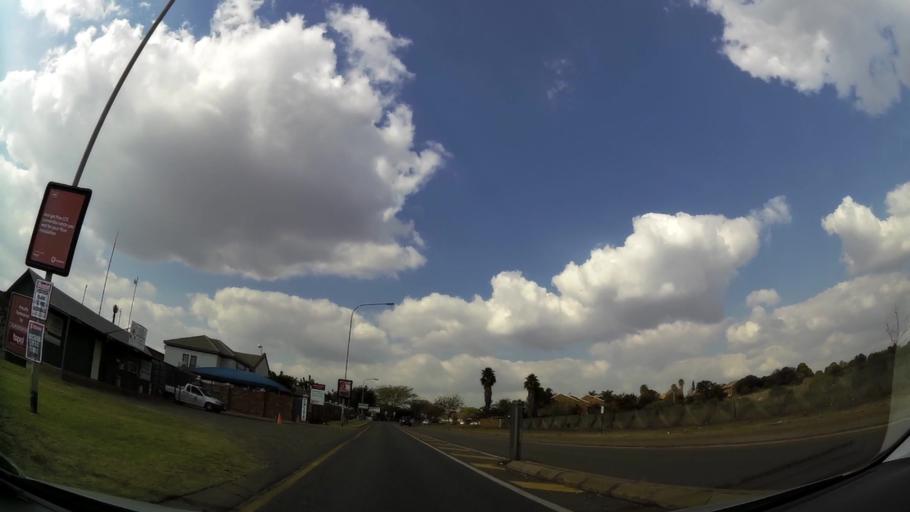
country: ZA
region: Gauteng
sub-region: City of Tshwane Metropolitan Municipality
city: Centurion
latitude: -25.8391
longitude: 28.2402
